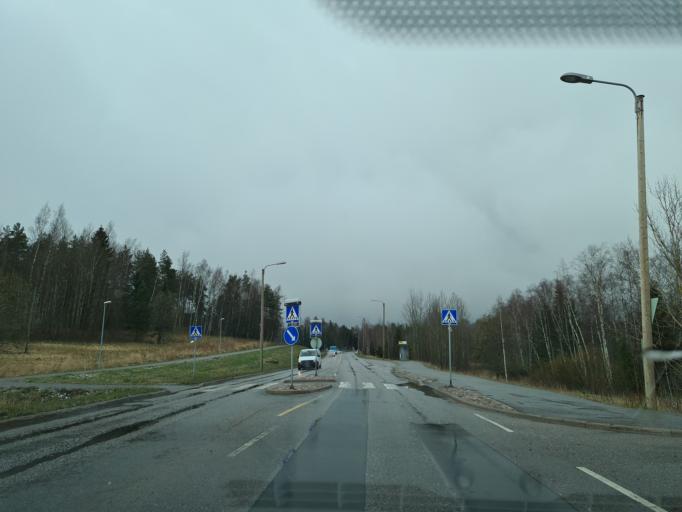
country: FI
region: Uusimaa
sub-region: Helsinki
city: Kirkkonummi
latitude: 60.0913
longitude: 24.4104
